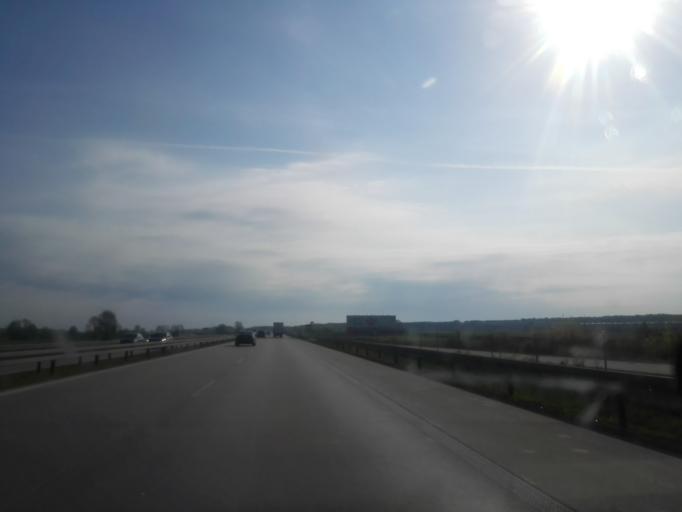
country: PL
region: Lodz Voivodeship
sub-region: Powiat piotrkowski
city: Wolborz
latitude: 51.4963
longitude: 19.8474
